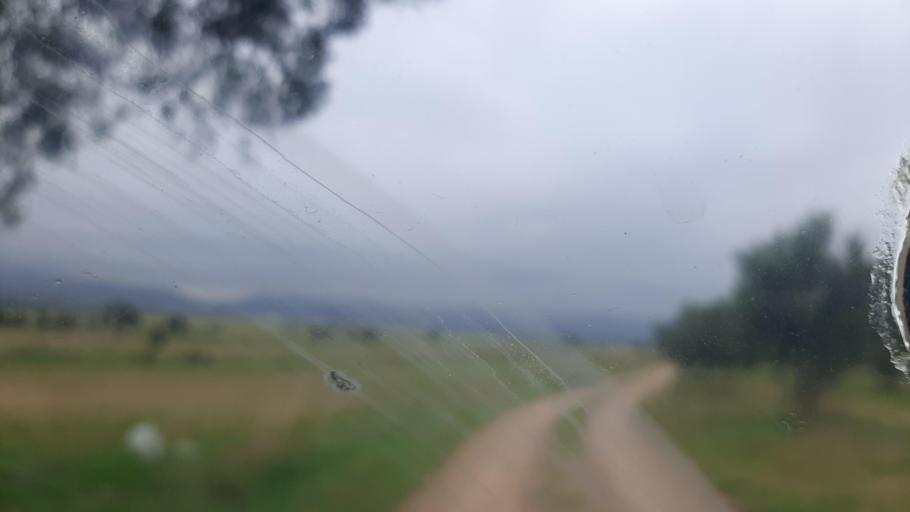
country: TN
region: Tunis
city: La Sebala du Mornag
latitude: 36.5716
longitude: 10.2939
